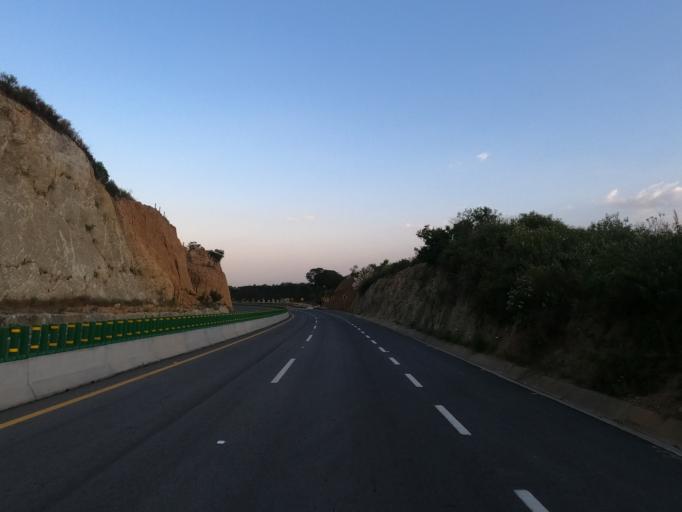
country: MX
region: Mexico
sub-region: Huixquilucan
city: Paraje Trejo (El Chaparral)
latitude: 19.4208
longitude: -99.3167
